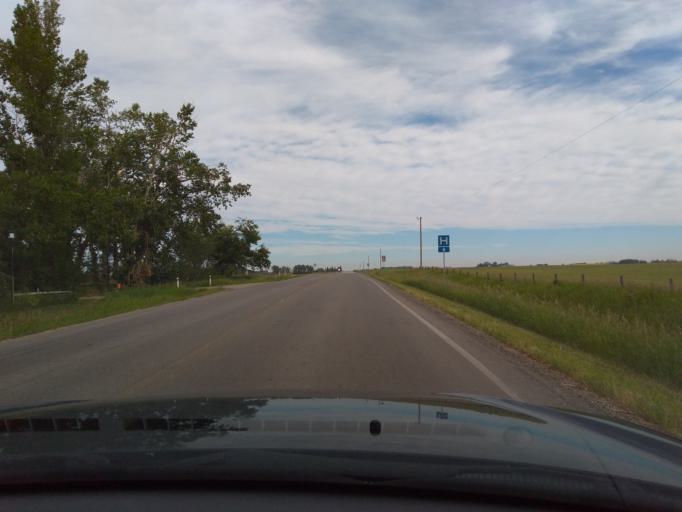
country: CA
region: Alberta
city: Carstairs
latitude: 51.5767
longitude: -114.1423
